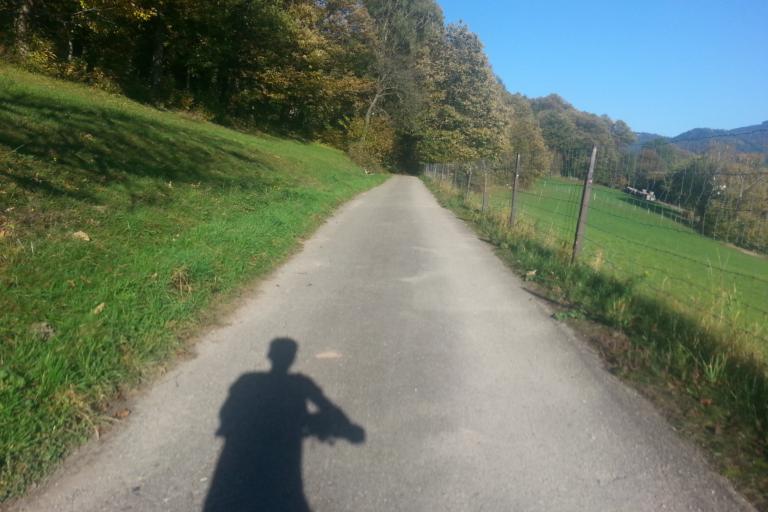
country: DE
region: Baden-Wuerttemberg
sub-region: Karlsruhe Region
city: Buhlertal
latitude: 48.6679
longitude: 8.1744
